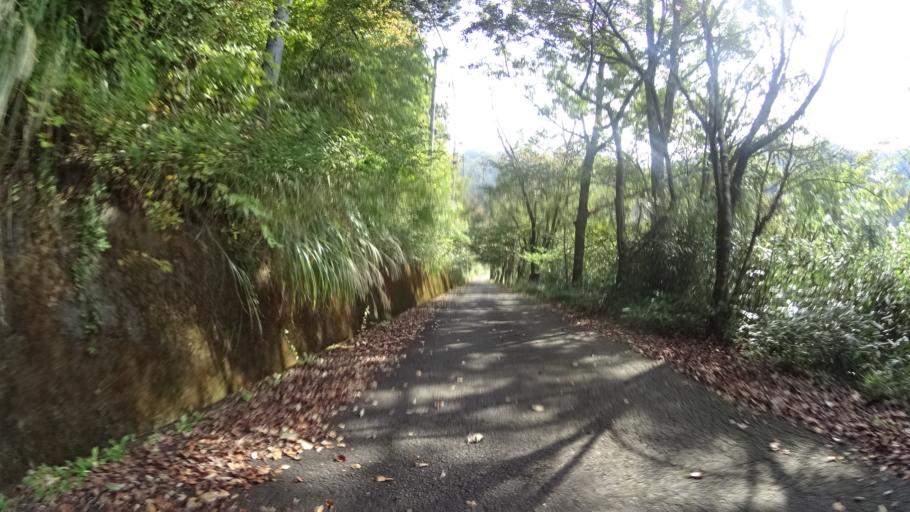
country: JP
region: Yamanashi
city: Otsuki
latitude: 35.5725
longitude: 138.9900
